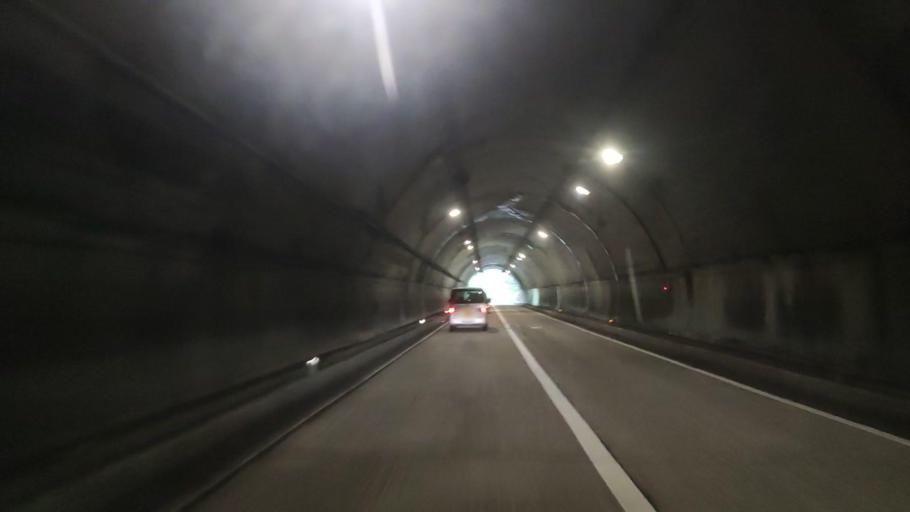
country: JP
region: Wakayama
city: Tanabe
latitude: 33.7804
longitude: 135.5043
